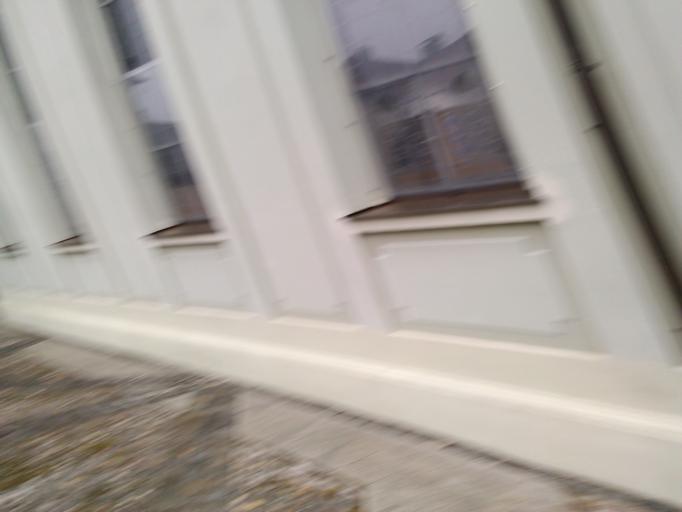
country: DE
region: Bavaria
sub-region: Swabia
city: Ichenhausen
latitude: 48.3706
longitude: 10.3065
